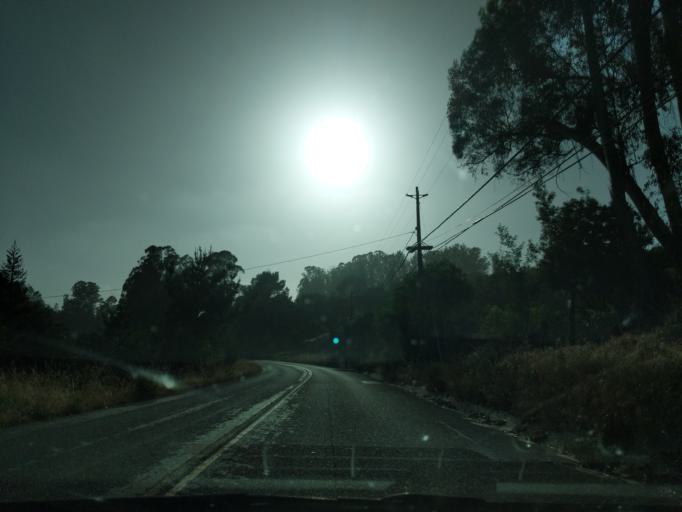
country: US
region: California
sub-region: Monterey County
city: Prunedale
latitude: 36.8256
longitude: -121.6551
